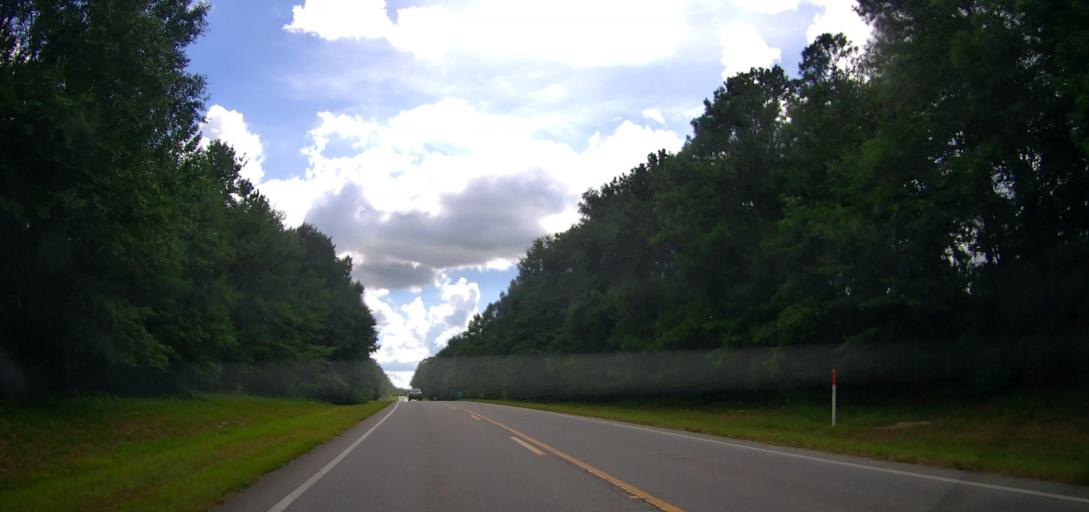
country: US
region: Alabama
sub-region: Russell County
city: Ladonia
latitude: 32.4433
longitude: -85.2905
